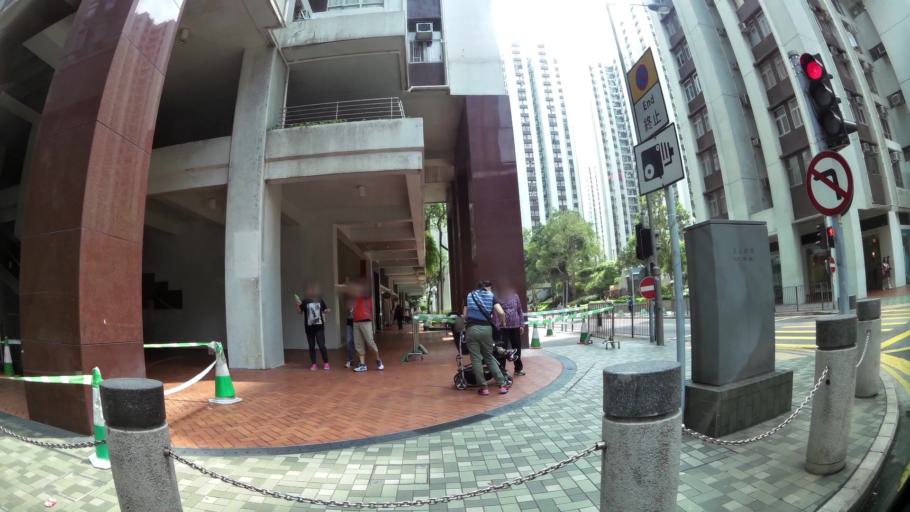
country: HK
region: Wanchai
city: Wan Chai
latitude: 22.2863
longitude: 114.2182
